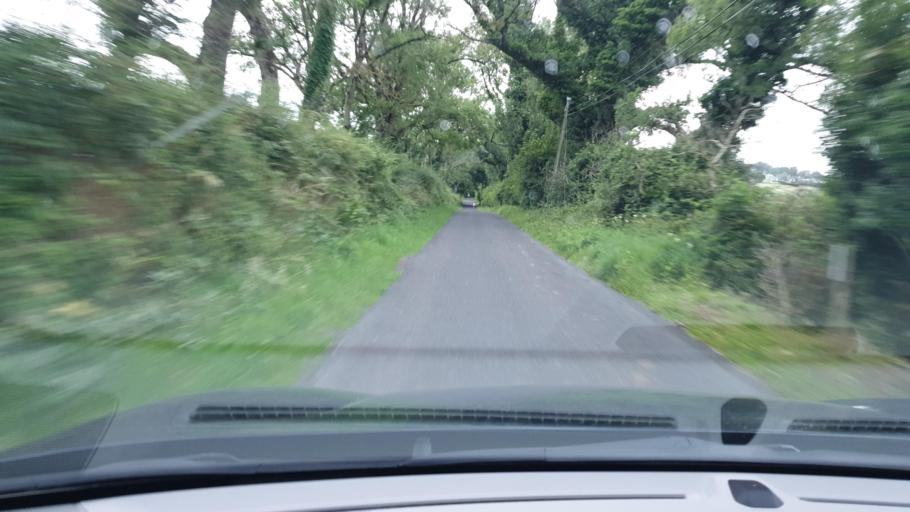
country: IE
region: Leinster
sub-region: Wicklow
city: Blessington
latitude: 53.2283
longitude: -6.5153
